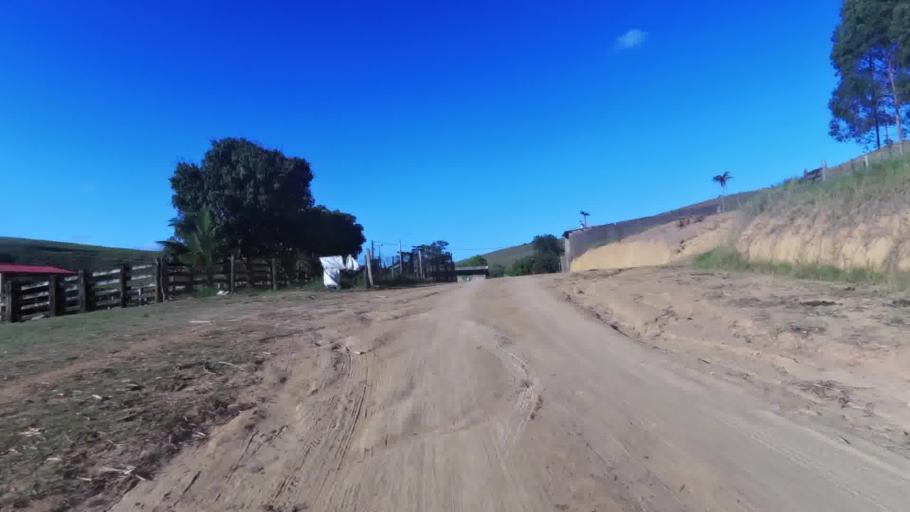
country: BR
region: Espirito Santo
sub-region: Marataizes
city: Marataizes
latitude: -21.1485
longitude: -41.0321
